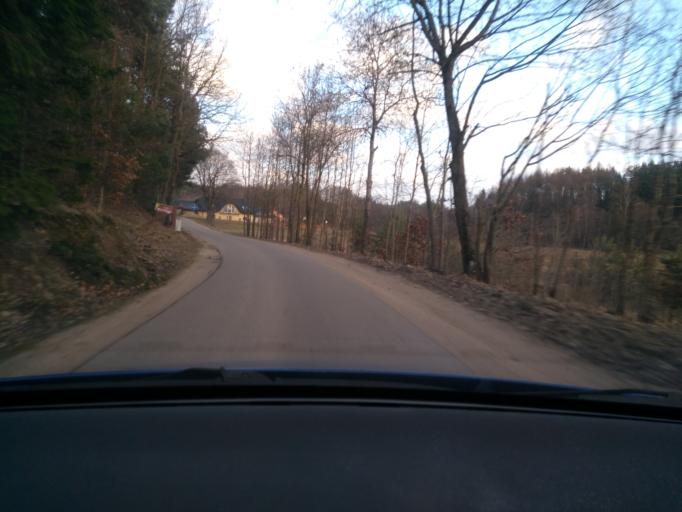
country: PL
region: Pomeranian Voivodeship
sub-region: Powiat kartuski
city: Przodkowo
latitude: 54.4150
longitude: 18.2445
